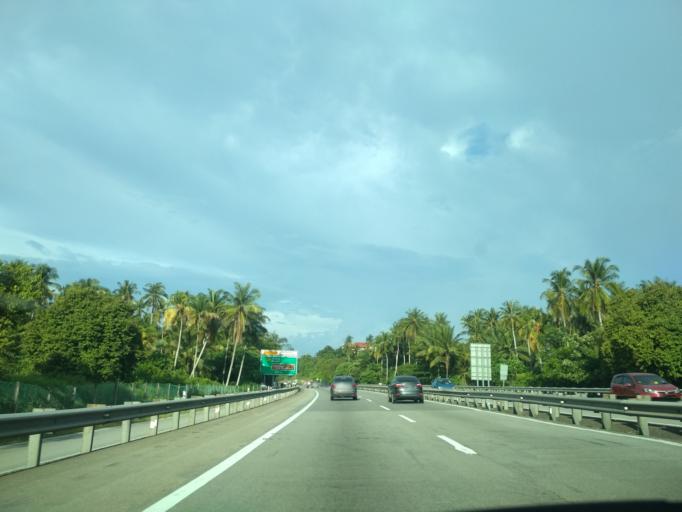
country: MY
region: Penang
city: Bukit Mertajam
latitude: 5.4036
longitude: 100.4778
